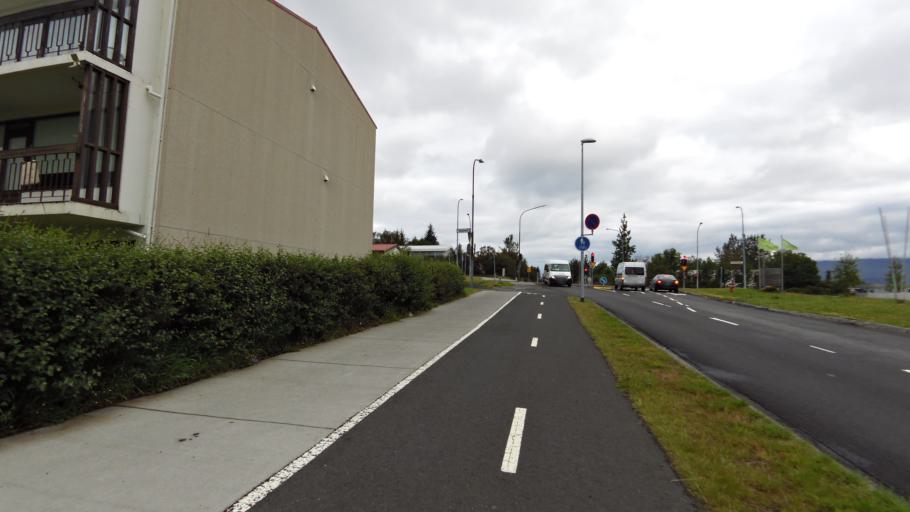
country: IS
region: Capital Region
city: Reykjavik
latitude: 64.1199
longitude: -21.8538
